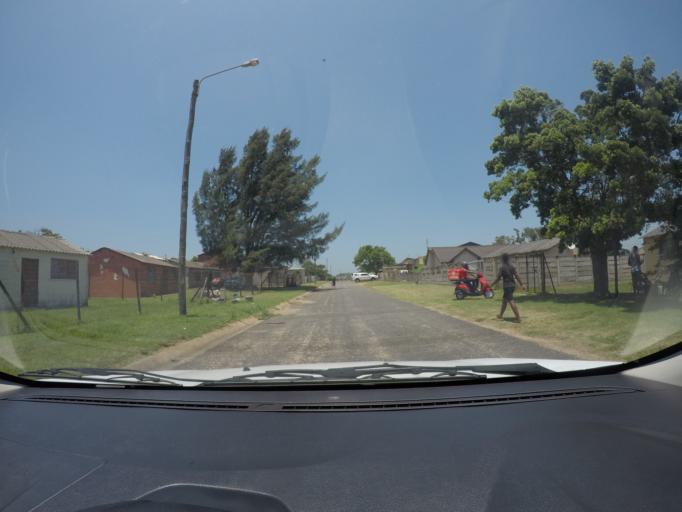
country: ZA
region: KwaZulu-Natal
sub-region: uThungulu District Municipality
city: eSikhawini
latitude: -28.8726
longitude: 31.9032
